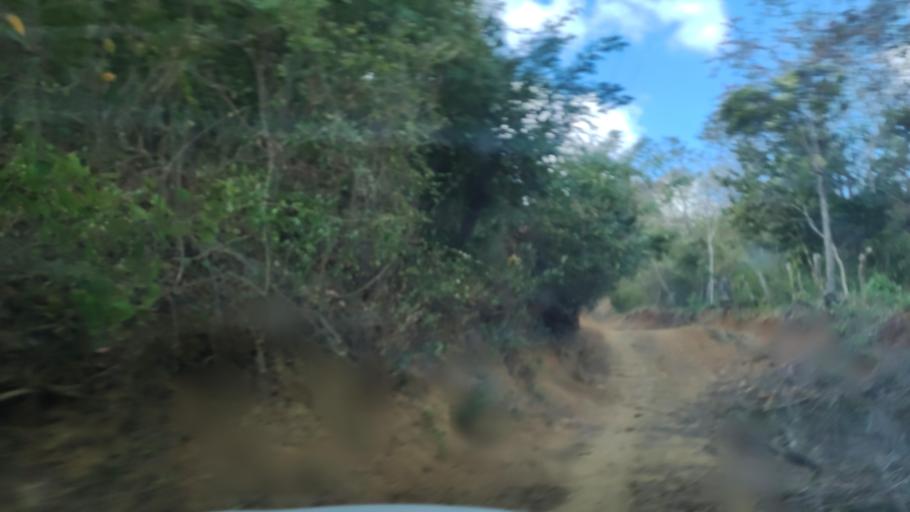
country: NI
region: Carazo
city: Santa Teresa
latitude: 11.6524
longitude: -86.1997
